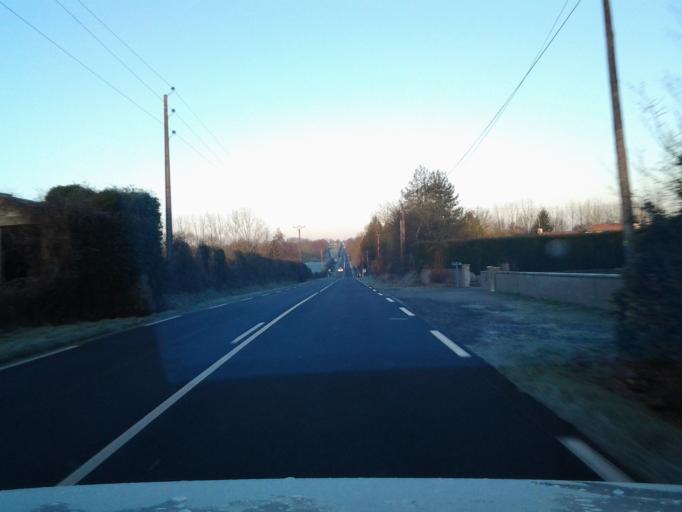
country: FR
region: Pays de la Loire
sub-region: Departement de la Vendee
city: Les Landes-Genusson
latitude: 46.9562
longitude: -1.0945
